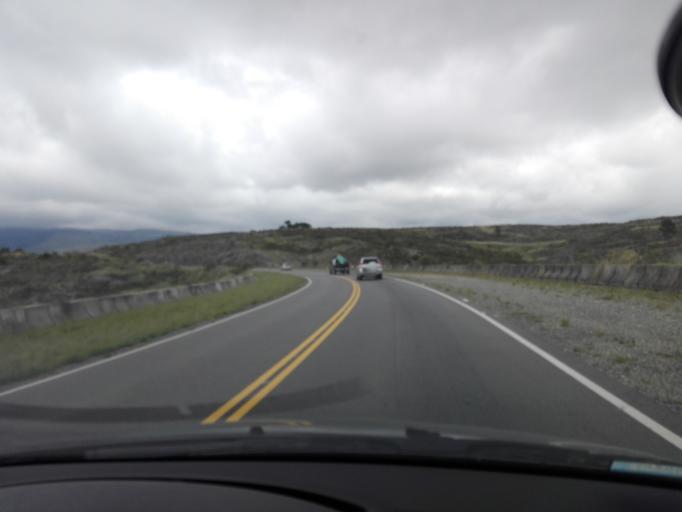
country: AR
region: Cordoba
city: Cuesta Blanca
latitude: -31.5705
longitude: -64.6495
